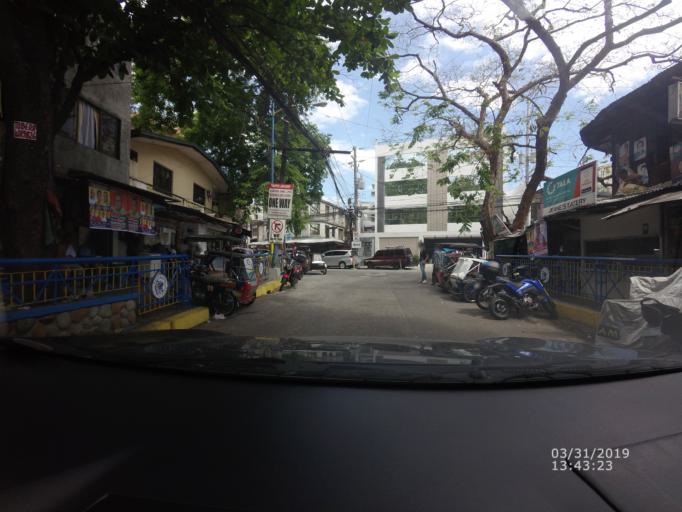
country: PH
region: Metro Manila
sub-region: Mandaluyong
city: Mandaluyong City
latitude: 14.5810
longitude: 121.0478
